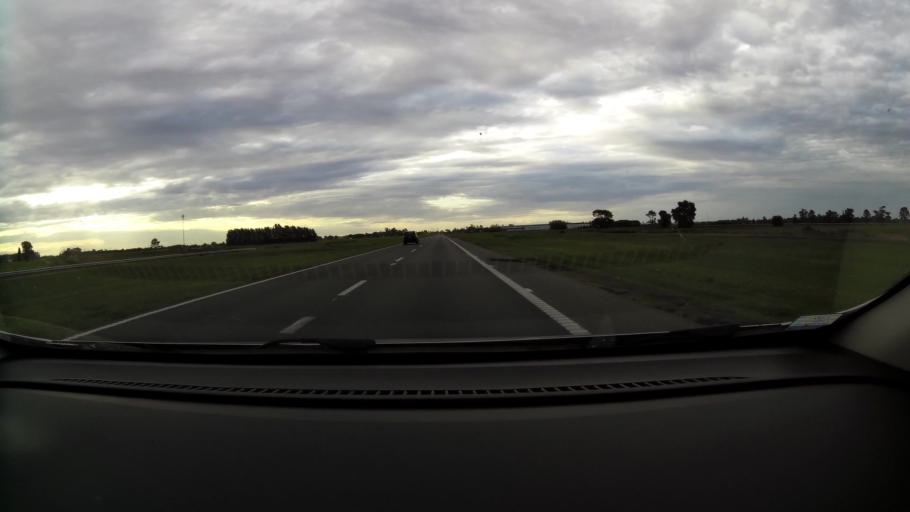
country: AR
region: Buenos Aires
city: San Nicolas de los Arroyos
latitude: -33.3968
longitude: -60.2093
